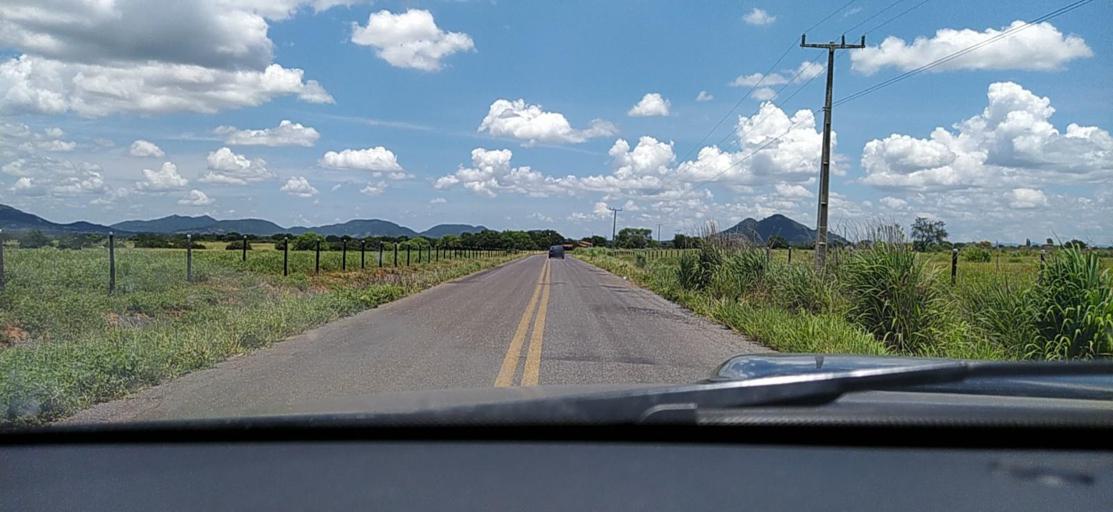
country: BR
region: Bahia
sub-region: Guanambi
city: Guanambi
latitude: -14.1013
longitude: -42.8703
